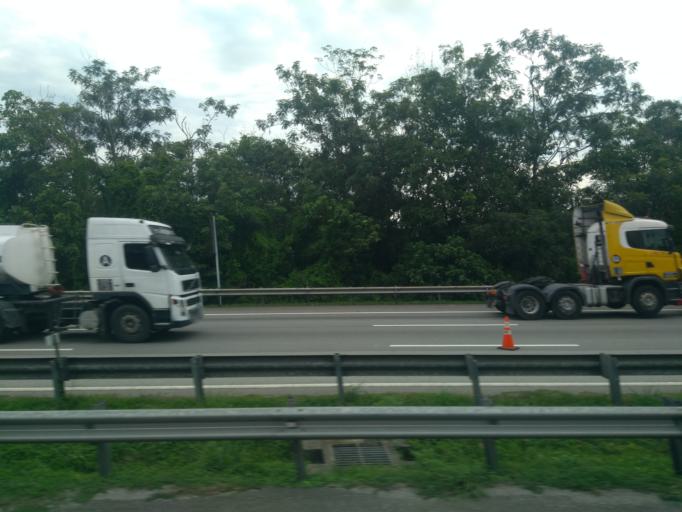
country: MY
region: Melaka
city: Pulau Sebang
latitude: 2.4218
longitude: 102.2142
